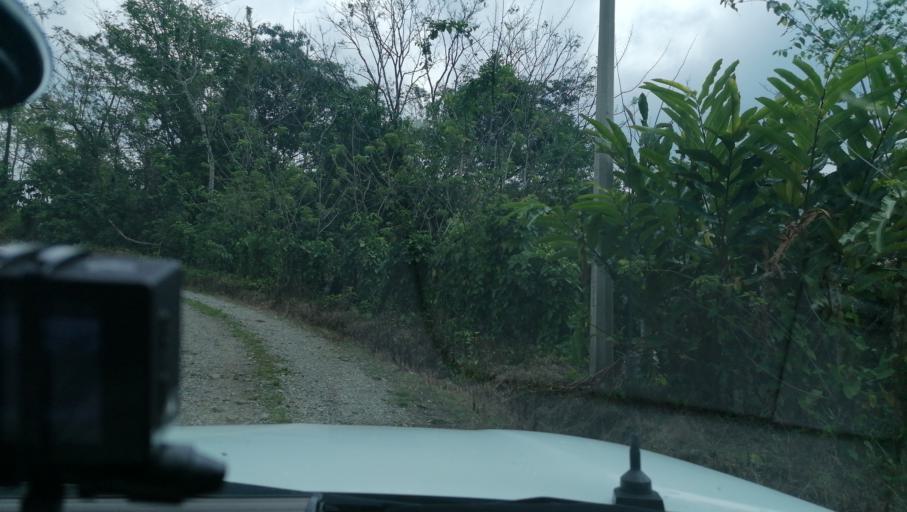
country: MX
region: Chiapas
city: Pichucalco
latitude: 17.4534
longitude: -93.2012
